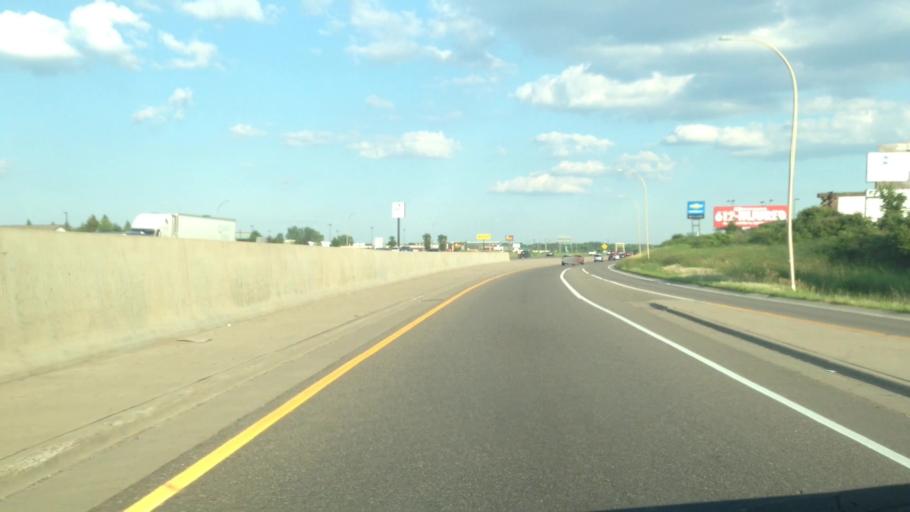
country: US
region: Minnesota
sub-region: Hennepin County
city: Rogers
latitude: 45.1935
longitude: -93.5499
